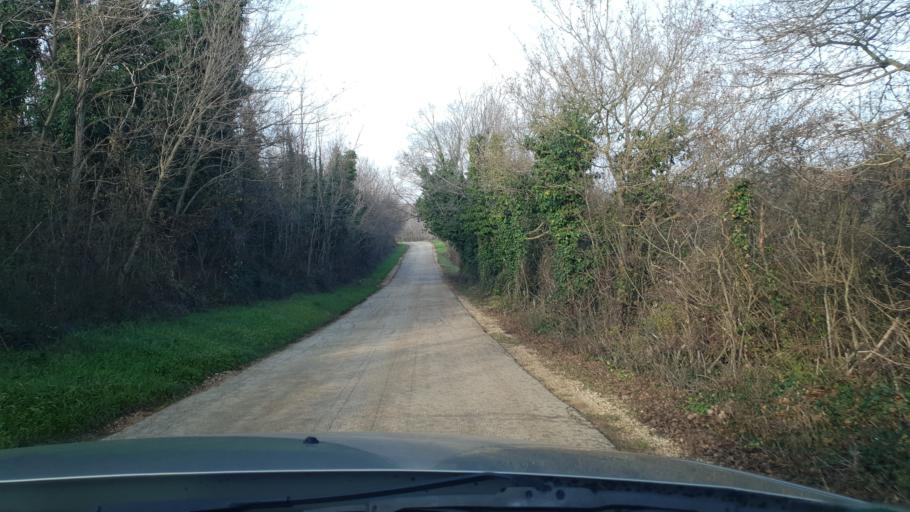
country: HR
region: Istarska
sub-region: Grad Porec
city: Porec
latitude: 45.2459
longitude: 13.6612
